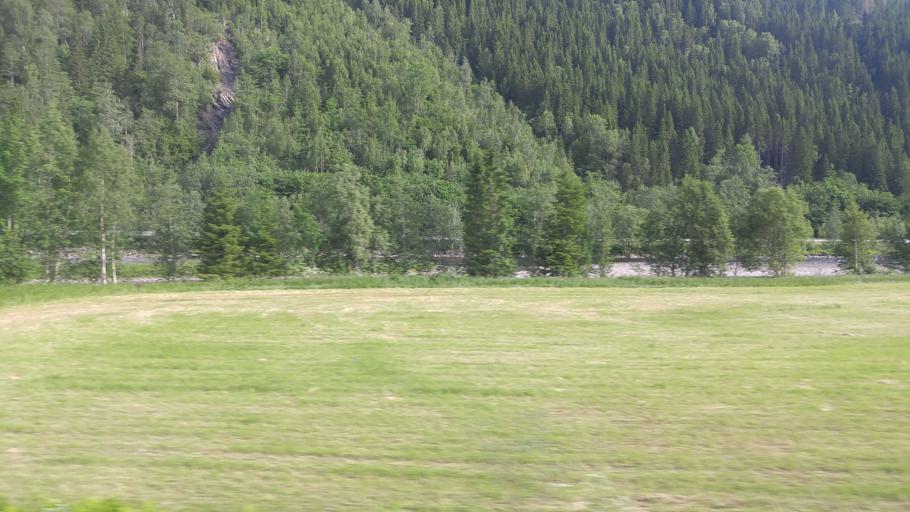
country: NO
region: Nord-Trondelag
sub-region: Levanger
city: Skogn
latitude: 63.4585
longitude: 11.3129
